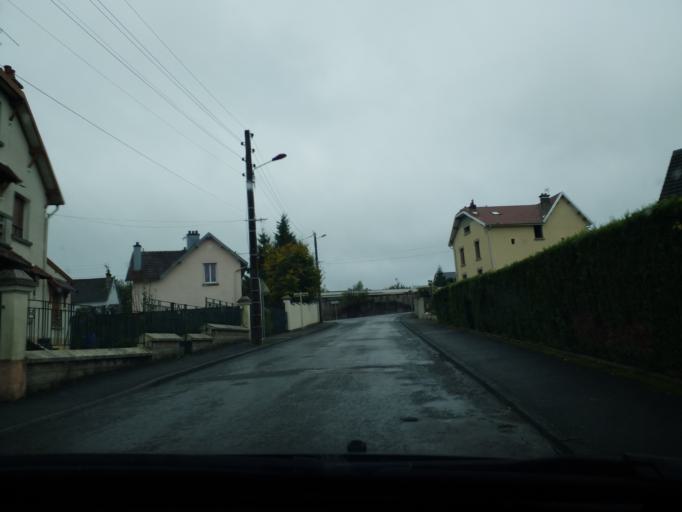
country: FR
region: Franche-Comte
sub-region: Departement de la Haute-Saone
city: Saint-Sauveur
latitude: 47.8164
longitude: 6.3880
